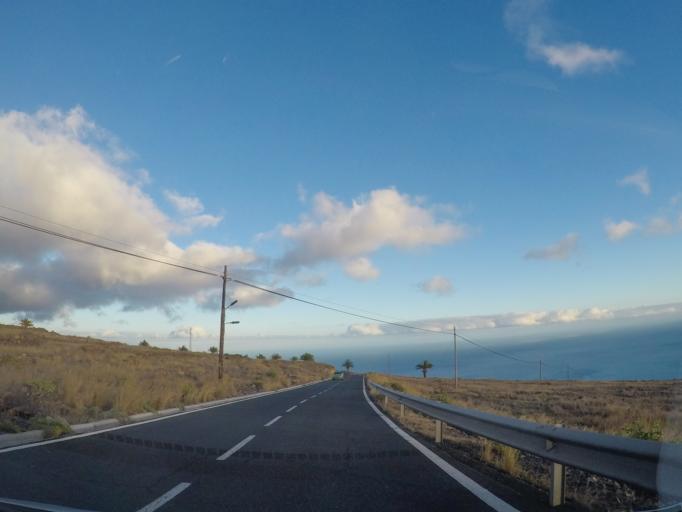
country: ES
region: Canary Islands
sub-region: Provincia de Santa Cruz de Tenerife
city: Alajero
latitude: 28.0486
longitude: -17.2325
